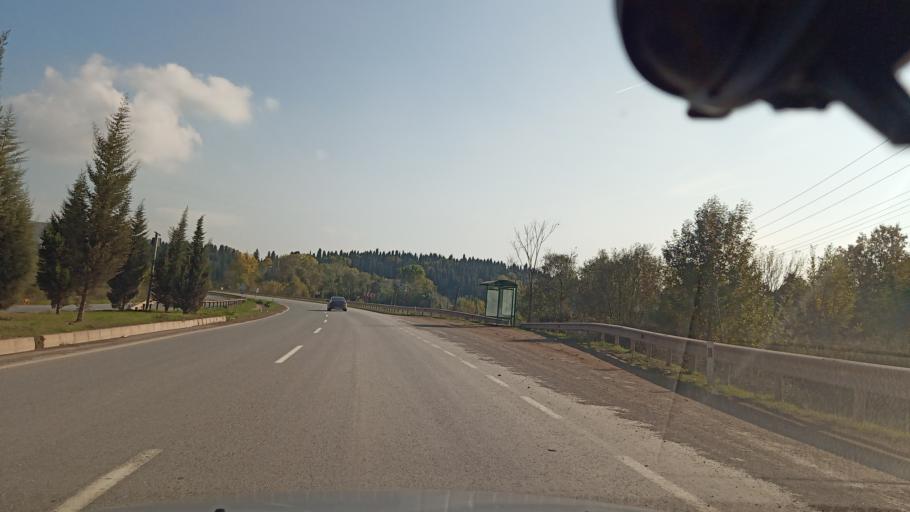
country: TR
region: Sakarya
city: Adapazari
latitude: 40.8289
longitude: 30.3809
